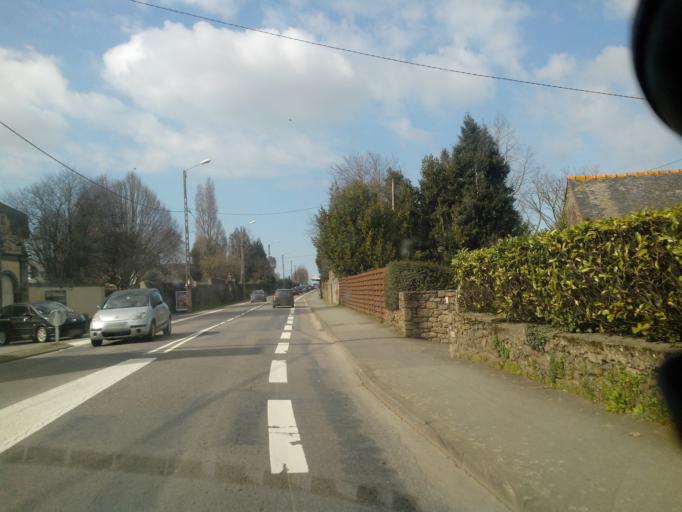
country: FR
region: Brittany
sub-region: Departement d'Ille-et-Vilaine
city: Saint-Malo
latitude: 48.6233
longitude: -1.9975
